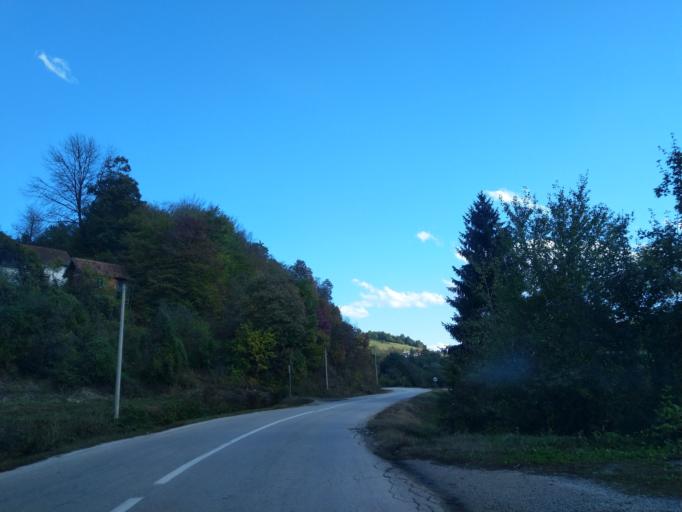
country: RS
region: Central Serbia
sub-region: Zlatiborski Okrug
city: Uzice
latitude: 43.8779
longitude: 19.7889
